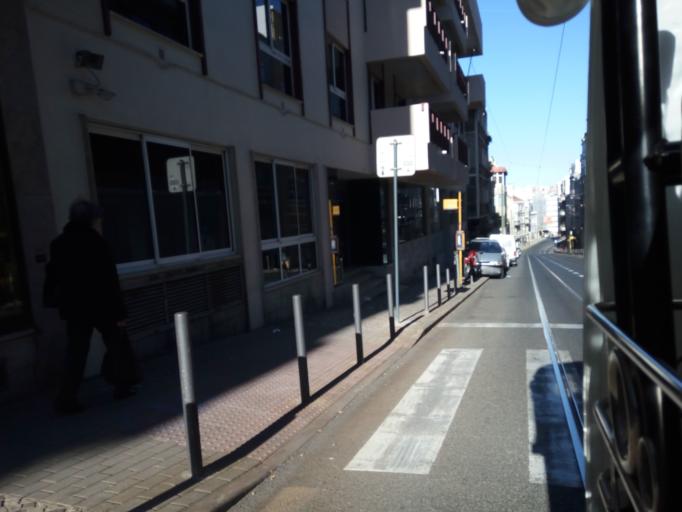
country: PT
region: Lisbon
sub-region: Lisbon
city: Lisbon
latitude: 38.7222
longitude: -9.1310
